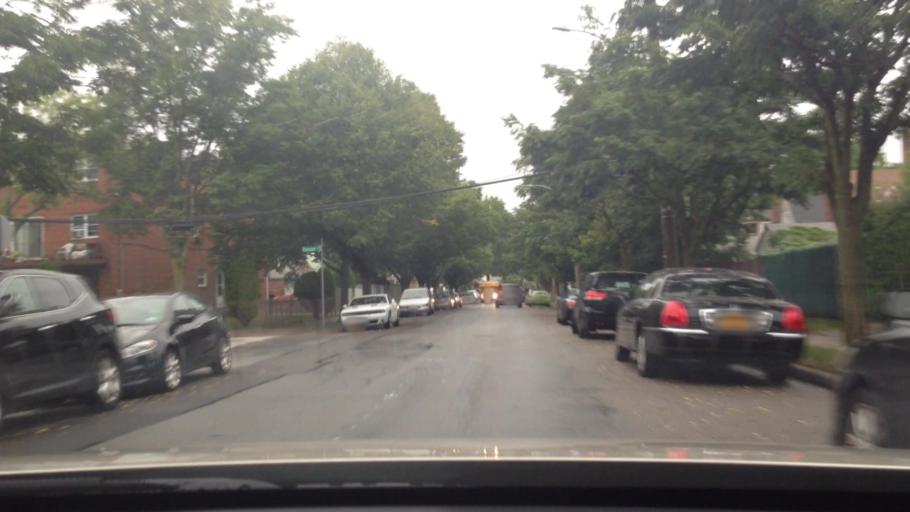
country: US
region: New York
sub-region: Nassau County
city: Bellerose Terrace
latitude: 40.7306
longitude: -73.7342
